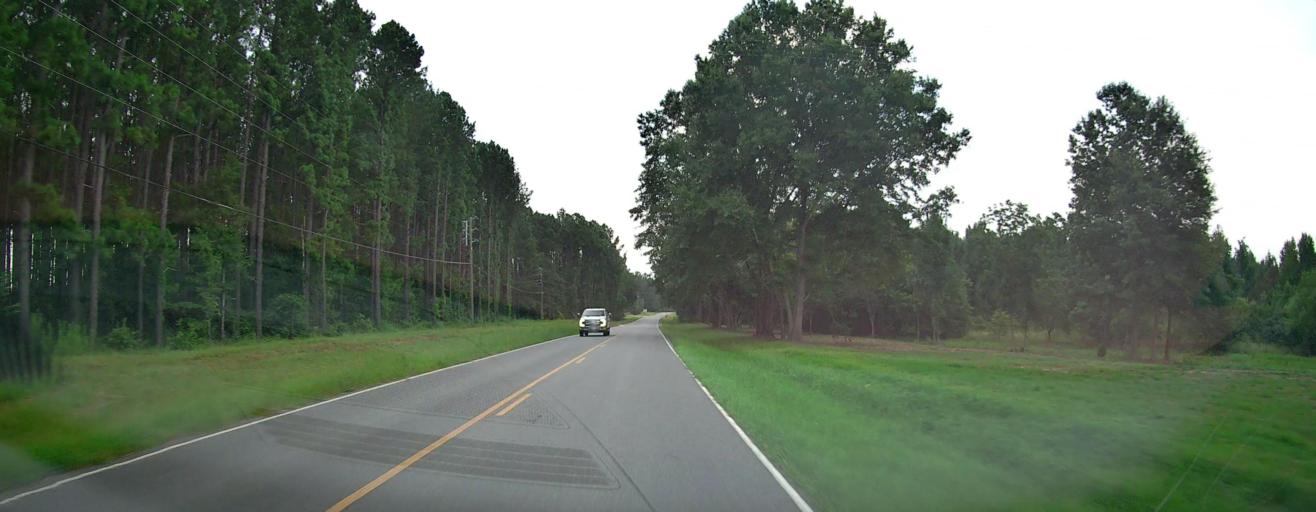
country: US
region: Georgia
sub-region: Laurens County
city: Dublin
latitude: 32.5836
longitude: -82.9027
